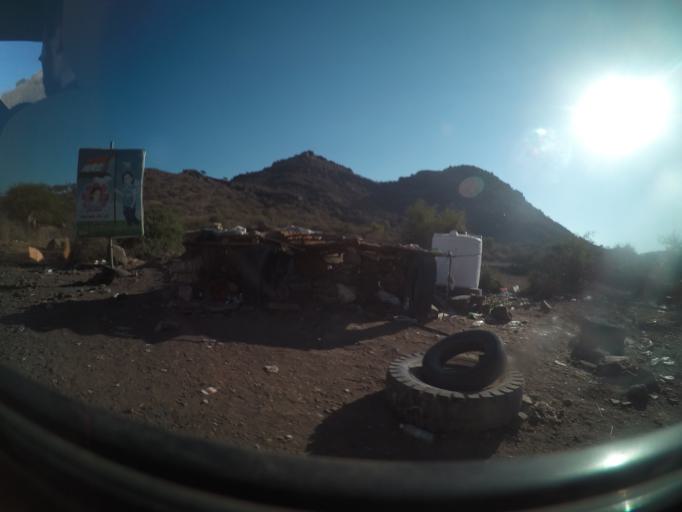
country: YE
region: Ad Dali'
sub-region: Ad Dhale'e
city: Dhalie
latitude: 13.6730
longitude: 44.7644
